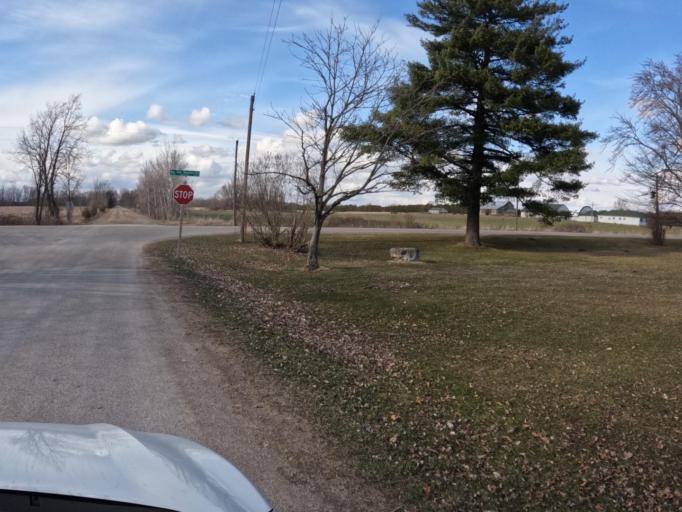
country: CA
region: Ontario
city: Brant
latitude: 43.0047
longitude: -80.4137
